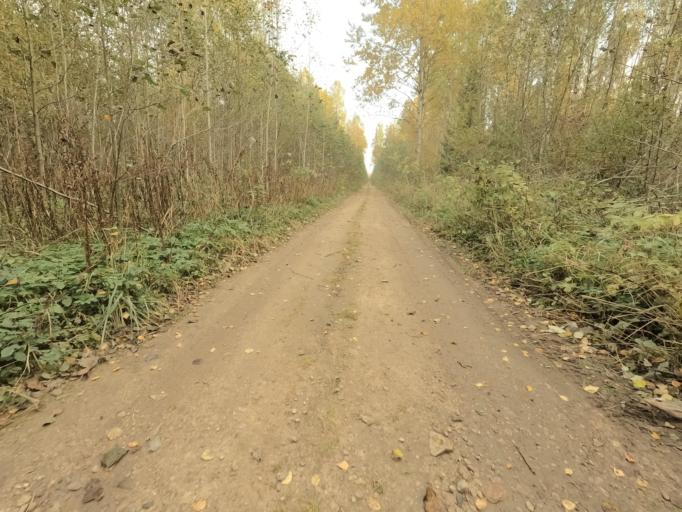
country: RU
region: Novgorod
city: Pankovka
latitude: 58.8801
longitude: 30.8314
